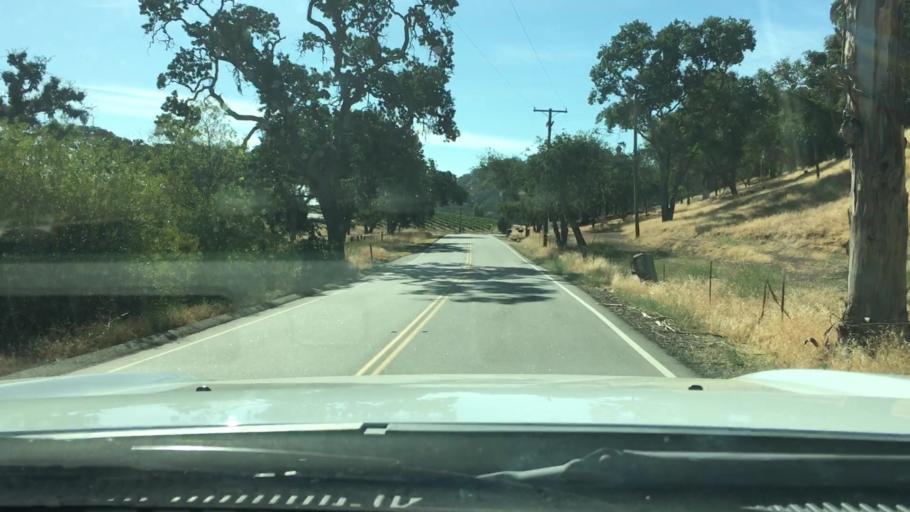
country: US
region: California
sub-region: San Luis Obispo County
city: Templeton
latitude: 35.5635
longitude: -120.6543
